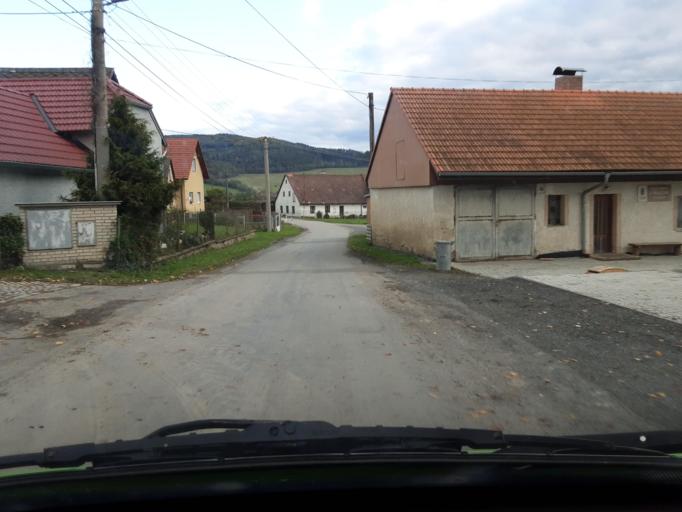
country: CZ
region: Plzensky
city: Janovice nad Uhlavou
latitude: 49.4190
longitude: 13.1607
